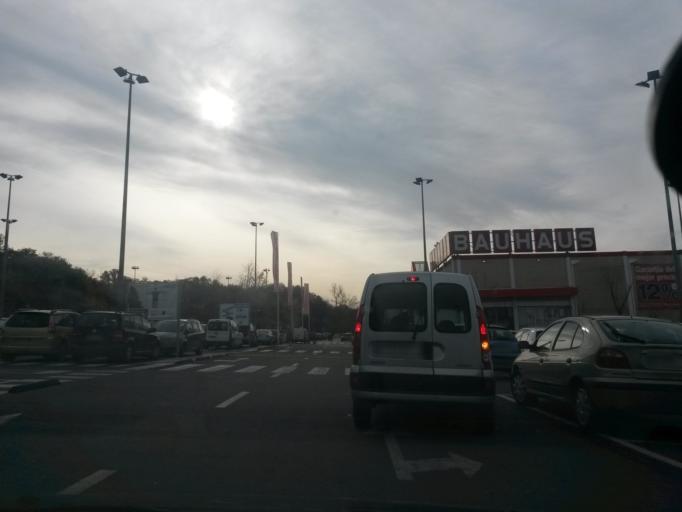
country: ES
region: Catalonia
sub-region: Provincia de Girona
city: Salt
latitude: 41.9598
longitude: 2.8120
